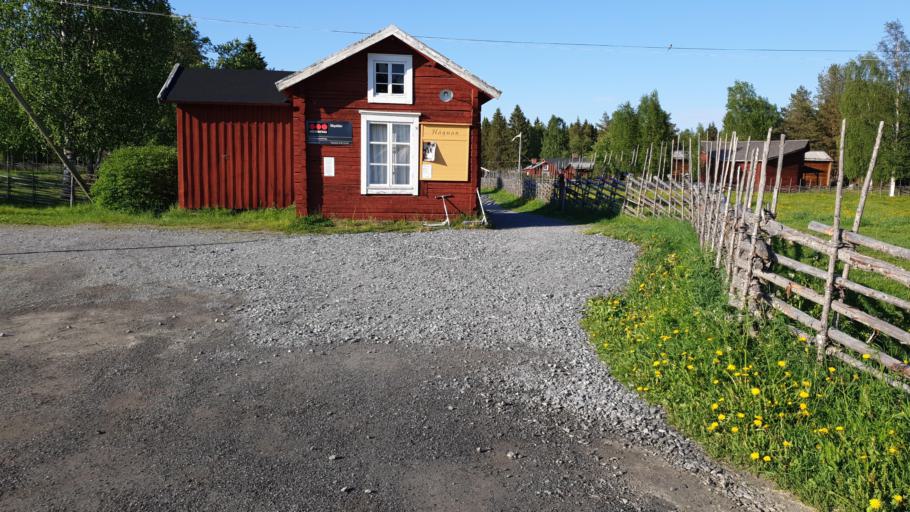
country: SE
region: Norrbotten
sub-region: Lulea Kommun
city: Gammelstad
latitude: 65.6478
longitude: 22.0341
